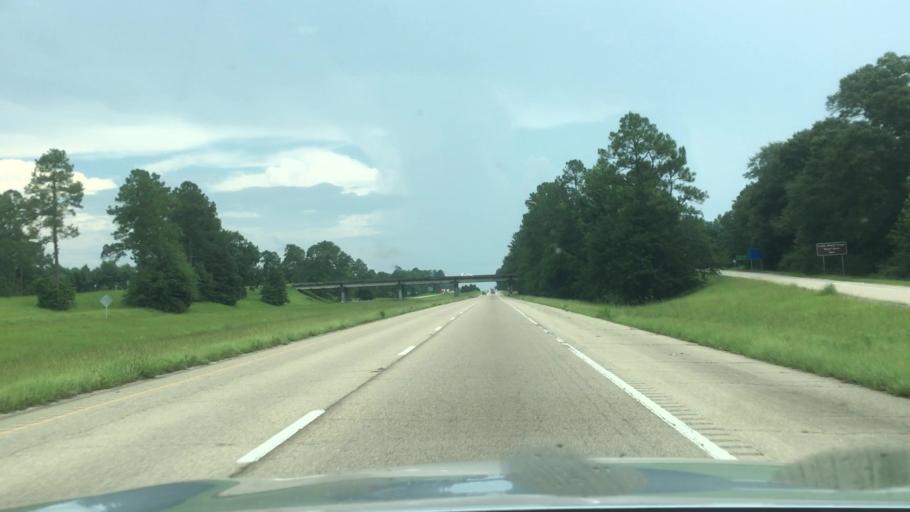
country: US
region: Mississippi
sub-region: Lamar County
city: Lumberton
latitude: 30.9984
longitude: -89.4197
